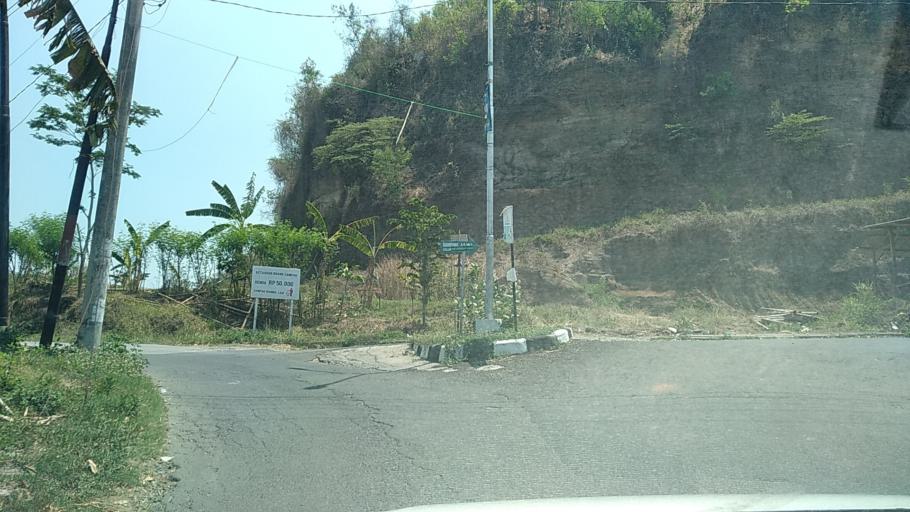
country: ID
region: Central Java
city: Semarang
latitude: -7.0230
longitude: 110.3789
